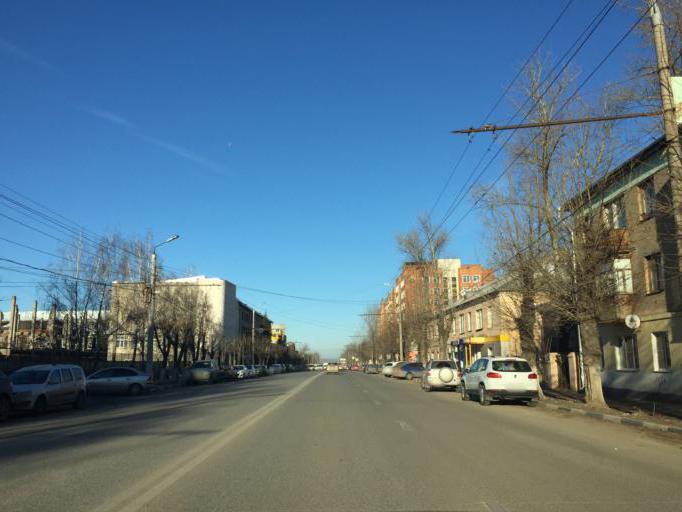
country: RU
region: Tula
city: Mendeleyevskiy
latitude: 54.1733
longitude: 37.5751
